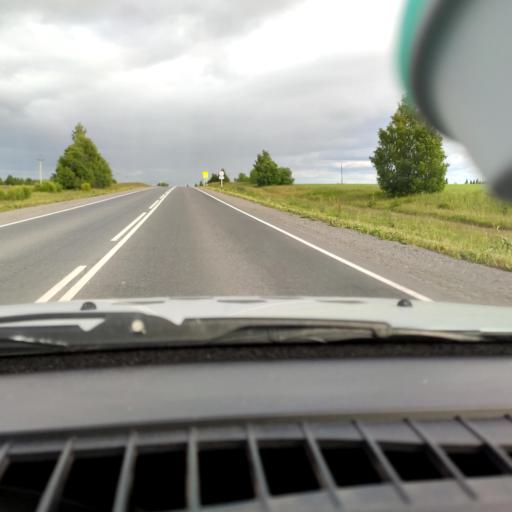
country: RU
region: Perm
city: Verkhnechusovskiye Gorodki
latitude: 58.2148
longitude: 57.1126
